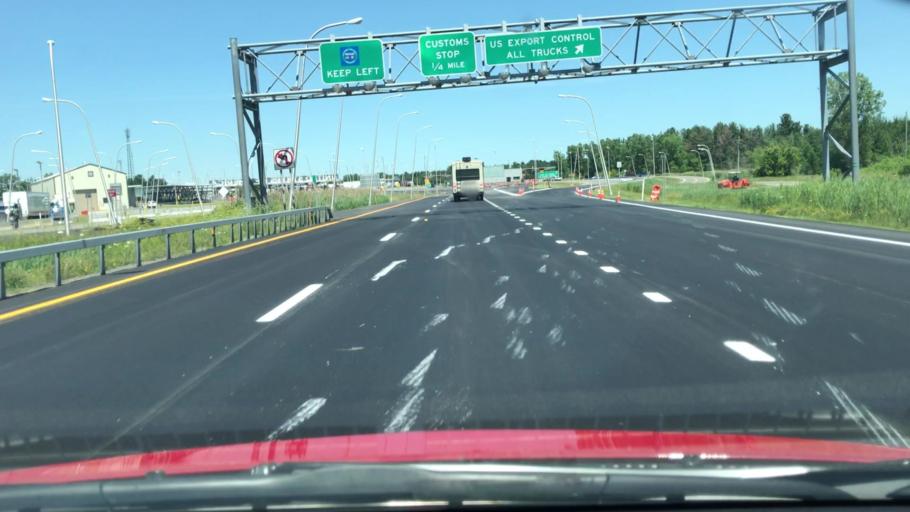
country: US
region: New York
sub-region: Clinton County
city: Champlain
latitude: 45.0027
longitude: -73.4532
